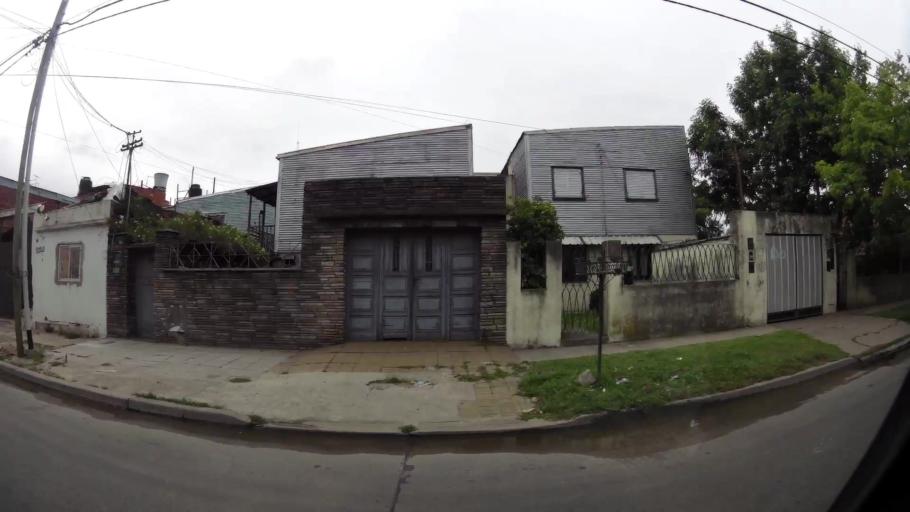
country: AR
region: Buenos Aires
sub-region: Partido de Avellaneda
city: Avellaneda
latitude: -34.6582
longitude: -58.3480
